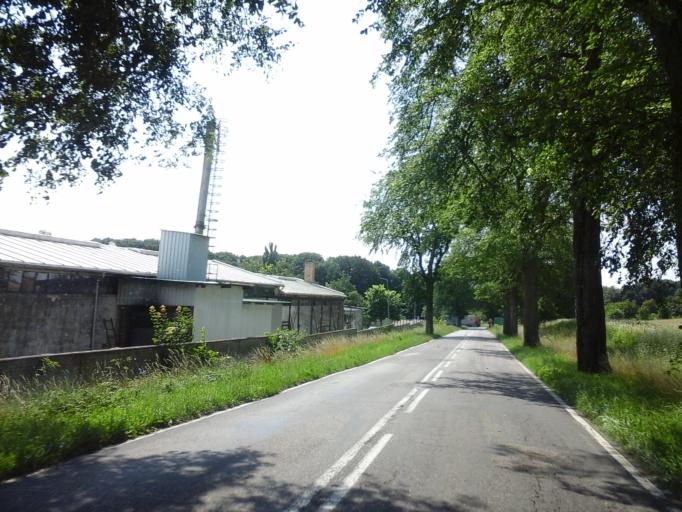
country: PL
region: West Pomeranian Voivodeship
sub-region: Powiat choszczenski
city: Recz
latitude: 53.2743
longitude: 15.5685
